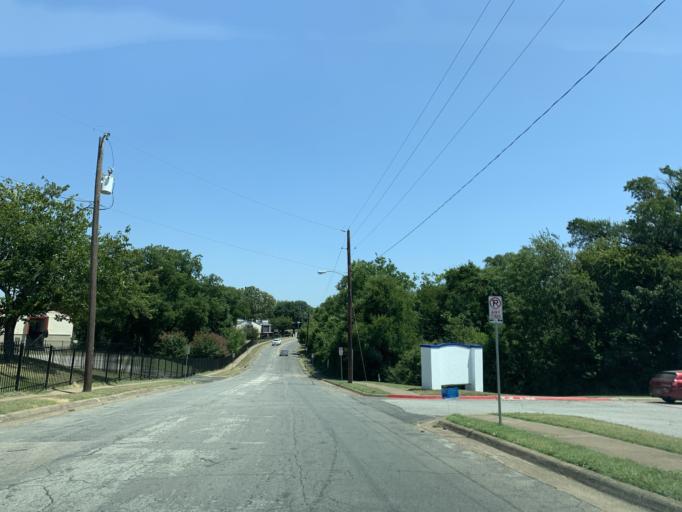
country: US
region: Texas
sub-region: Dallas County
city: Hutchins
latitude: 32.6752
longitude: -96.7662
